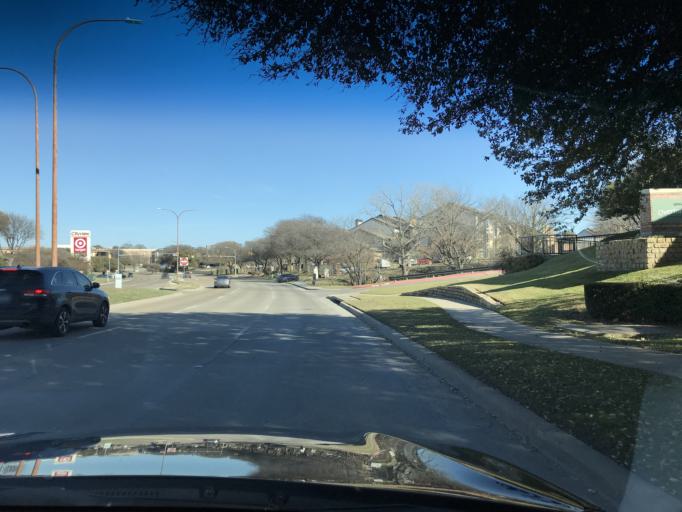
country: US
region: Texas
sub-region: Tarrant County
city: Benbrook
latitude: 32.6755
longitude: -97.4126
